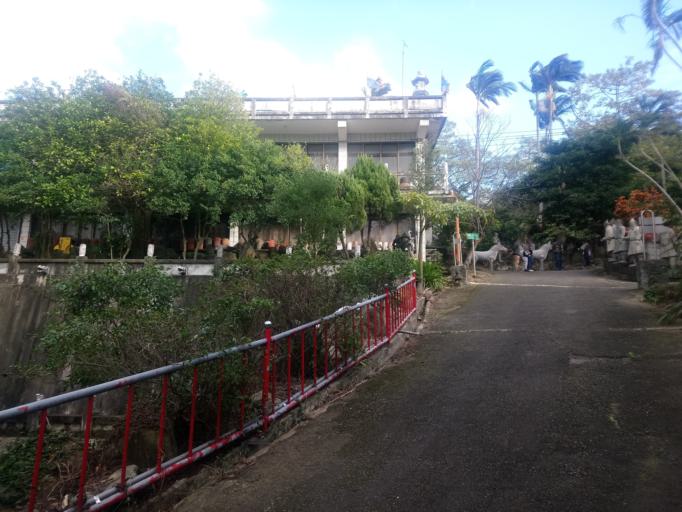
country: TW
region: Taiwan
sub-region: Hsinchu
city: Hsinchu
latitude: 24.7804
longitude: 120.9779
